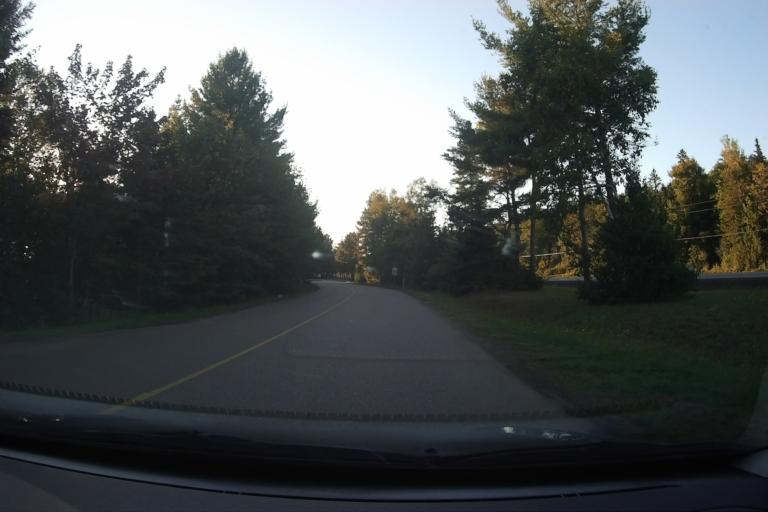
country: CA
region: Ontario
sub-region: Algoma
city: Sault Ste. Marie
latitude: 46.9679
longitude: -84.6796
